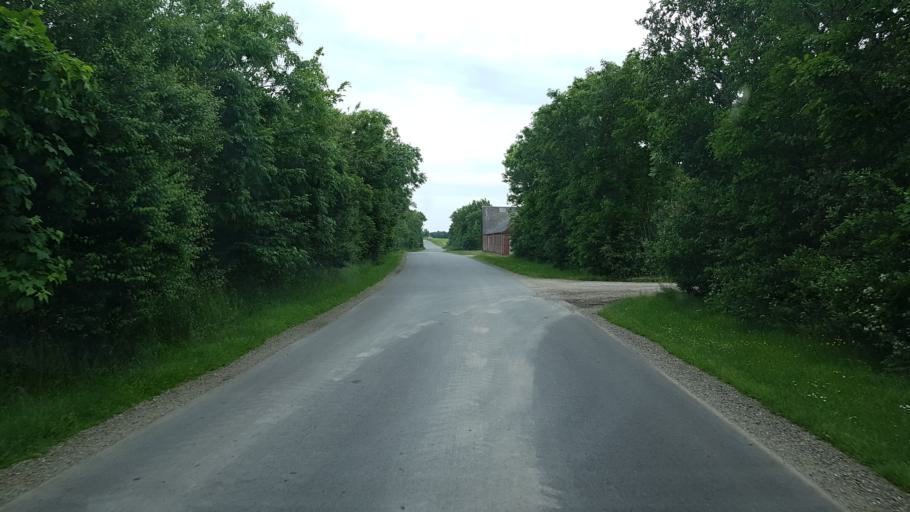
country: DK
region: South Denmark
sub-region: Varde Kommune
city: Oksbol
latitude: 55.7291
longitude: 8.3726
